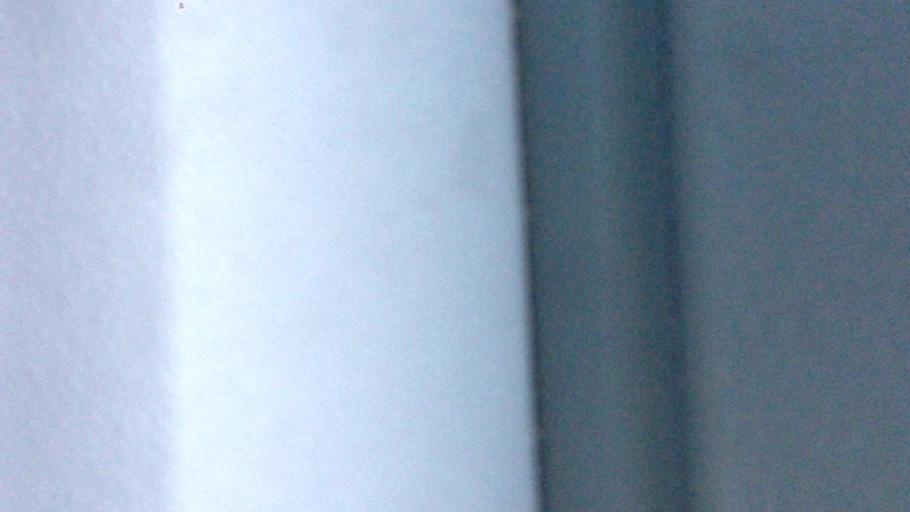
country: US
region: New York
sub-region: Dutchess County
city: Rhinebeck
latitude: 41.9682
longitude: -73.9216
